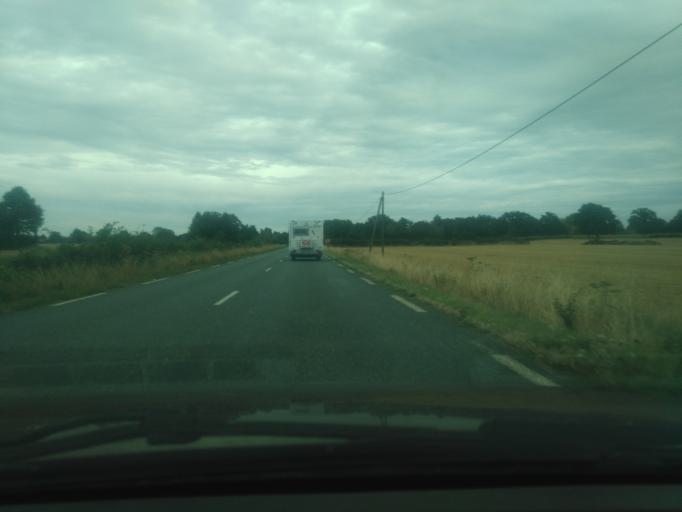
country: FR
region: Auvergne
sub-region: Departement de l'Allier
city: Ainay-le-Chateau
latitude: 46.7608
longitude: 2.8084
